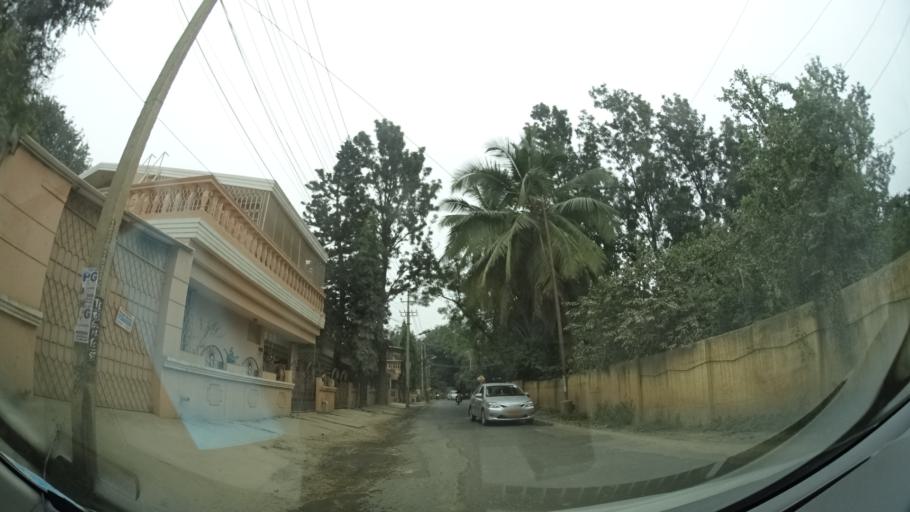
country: IN
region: Karnataka
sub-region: Bangalore Rural
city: Hoskote
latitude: 12.9739
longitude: 77.7470
